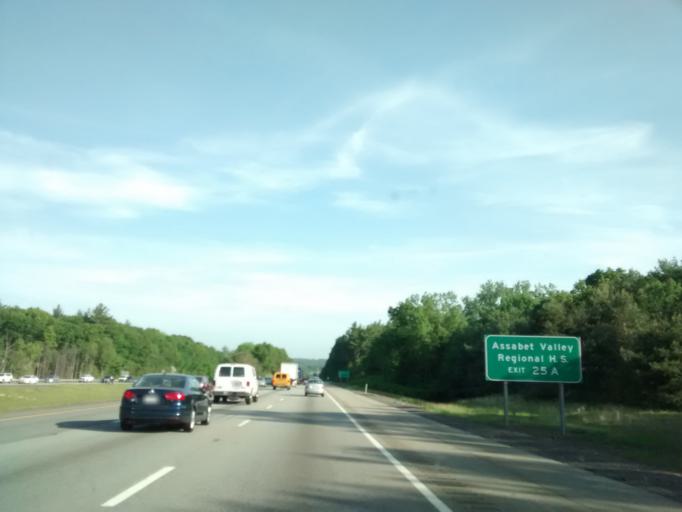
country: US
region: Massachusetts
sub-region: Worcester County
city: Berlin
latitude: 42.3851
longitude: -71.6036
